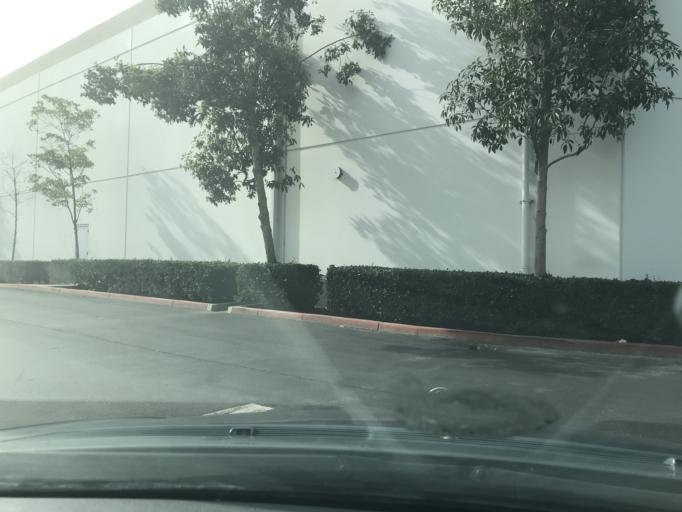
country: US
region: California
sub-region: Los Angeles County
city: Santa Fe Springs
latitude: 33.9334
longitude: -118.0625
